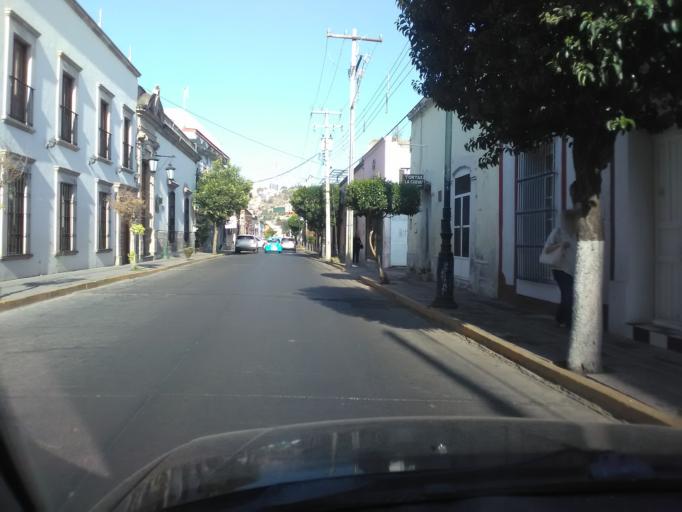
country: MX
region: Durango
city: Victoria de Durango
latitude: 24.0229
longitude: -104.6726
